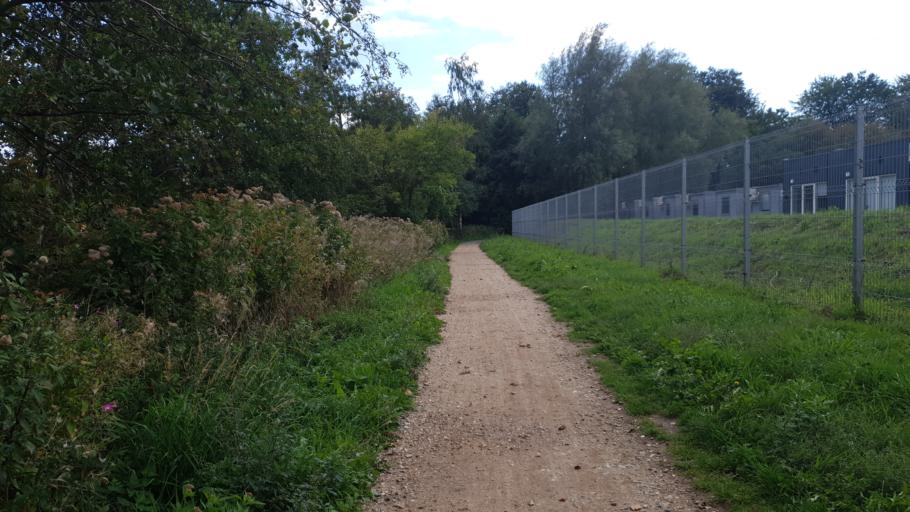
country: DK
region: South Denmark
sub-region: Fredericia Kommune
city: Snoghoj
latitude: 55.5523
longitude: 9.7228
